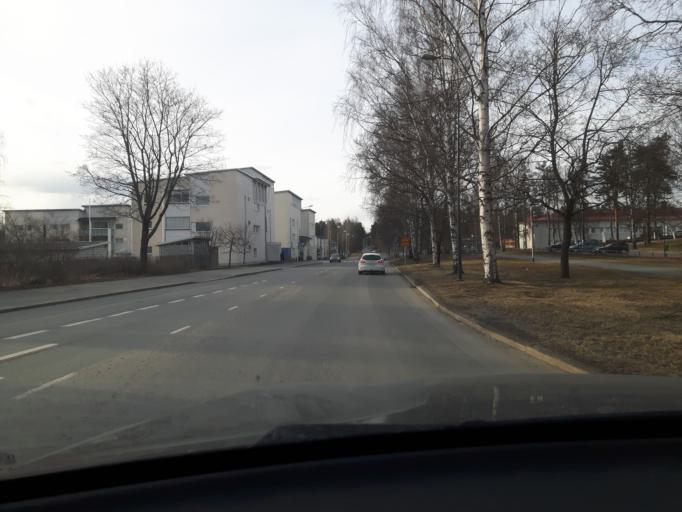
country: FI
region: Pirkanmaa
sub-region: Etelae-Pirkanmaa
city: Valkeakoski
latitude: 61.2688
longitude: 24.0304
